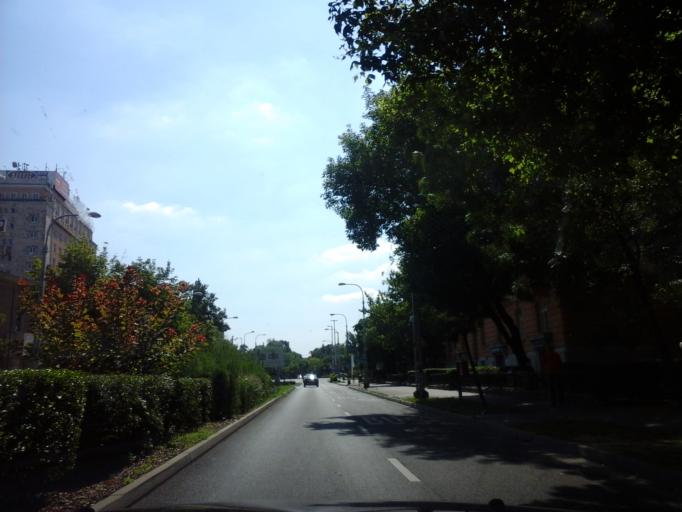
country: HU
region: Budapest
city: Budapest VIII. keruelet
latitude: 47.4829
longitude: 19.1013
